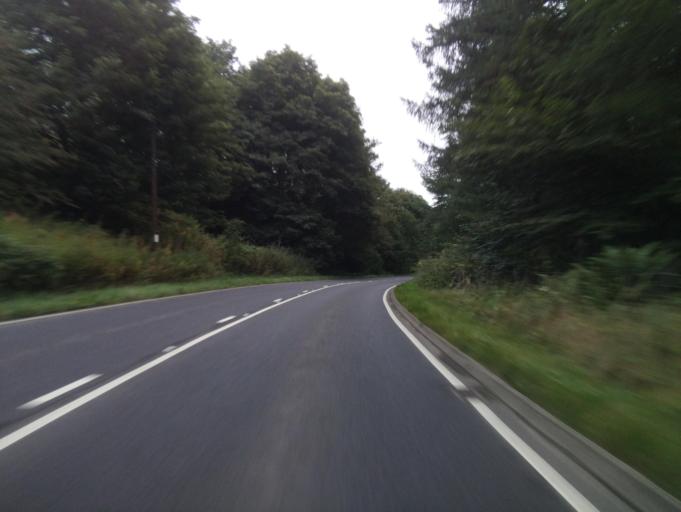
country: GB
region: Scotland
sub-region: Clackmannanshire
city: Dollar
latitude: 56.1805
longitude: -3.6289
